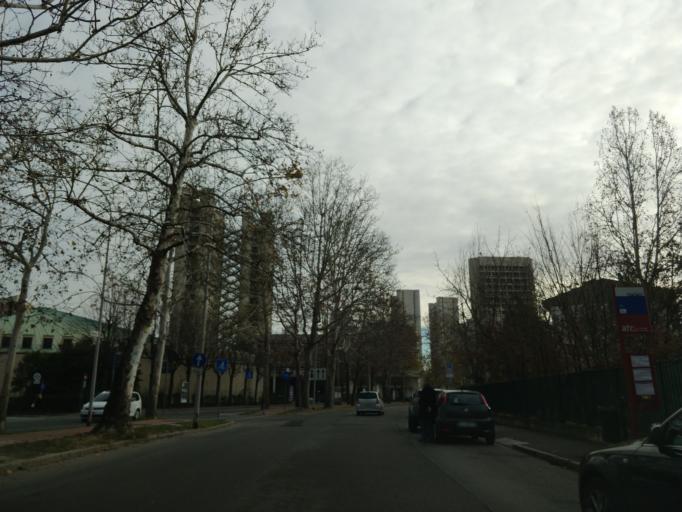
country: IT
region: Emilia-Romagna
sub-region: Provincia di Bologna
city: Bologna
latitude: 44.5102
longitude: 11.3606
